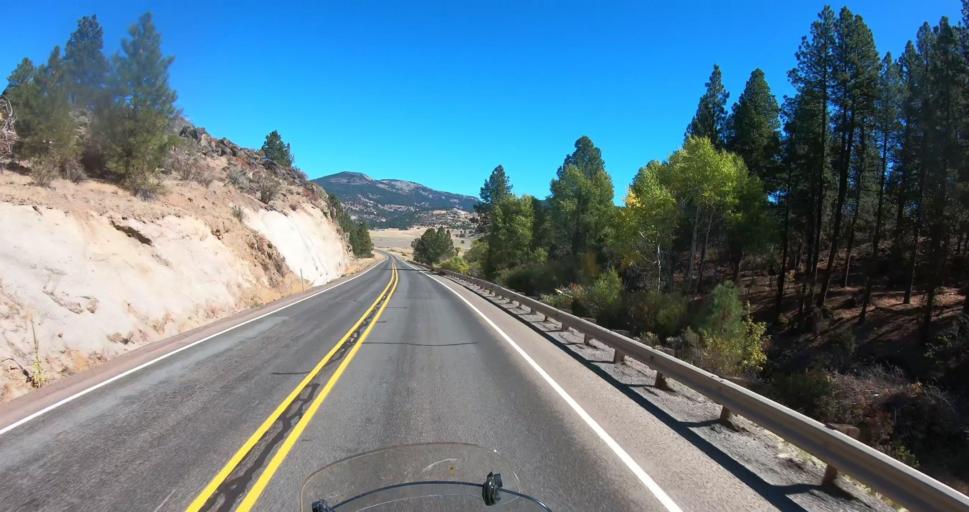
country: US
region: Oregon
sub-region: Lake County
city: Lakeview
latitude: 42.3257
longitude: -120.3096
